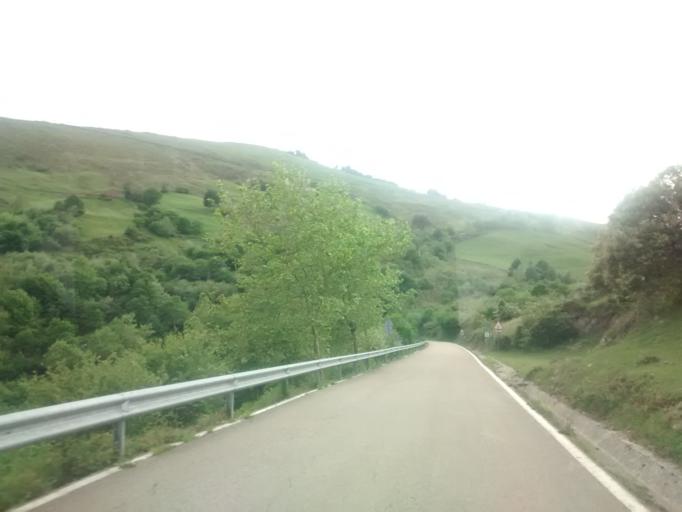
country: ES
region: Cantabria
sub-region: Provincia de Cantabria
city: San Vicente de la Barquera
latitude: 43.2560
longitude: -4.4407
